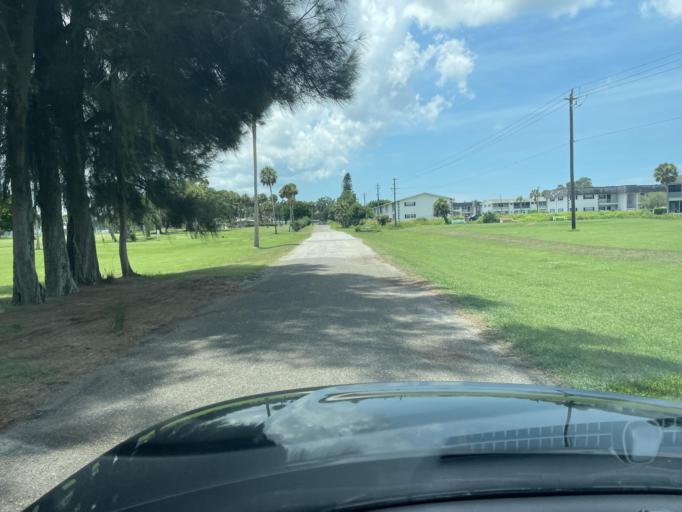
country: US
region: Florida
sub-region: Manatee County
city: West Samoset
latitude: 27.4592
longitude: -82.5630
